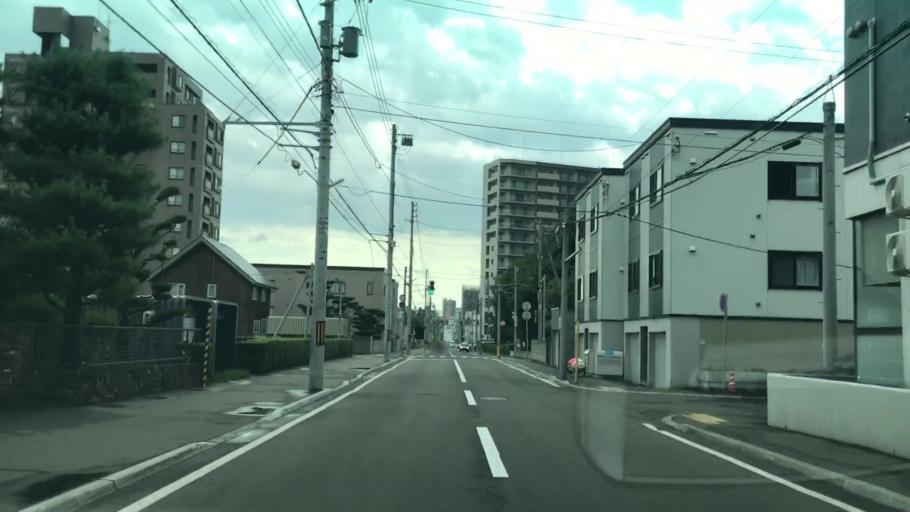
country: JP
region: Hokkaido
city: Sapporo
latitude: 43.0746
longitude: 141.3098
